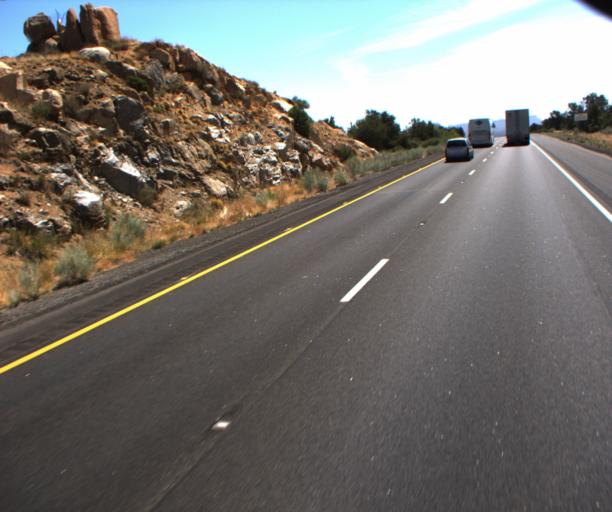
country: US
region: Arizona
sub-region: Mohave County
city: Peach Springs
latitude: 35.1840
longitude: -113.3968
